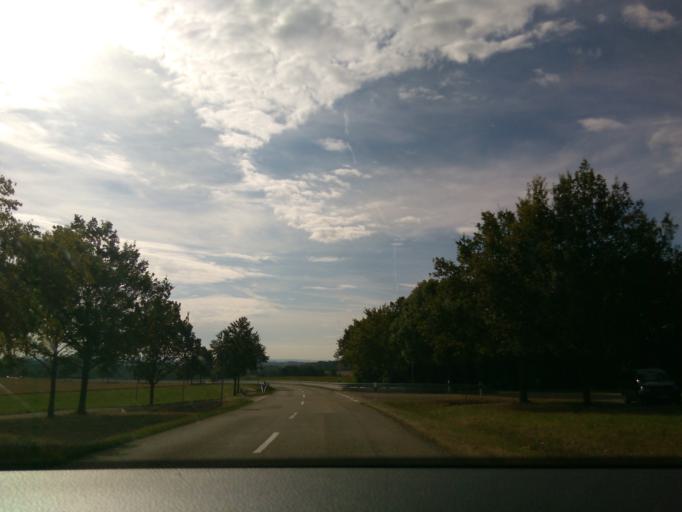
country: DE
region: Baden-Wuerttemberg
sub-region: Regierungsbezirk Stuttgart
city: Langenburg
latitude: 49.2456
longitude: 9.8779
